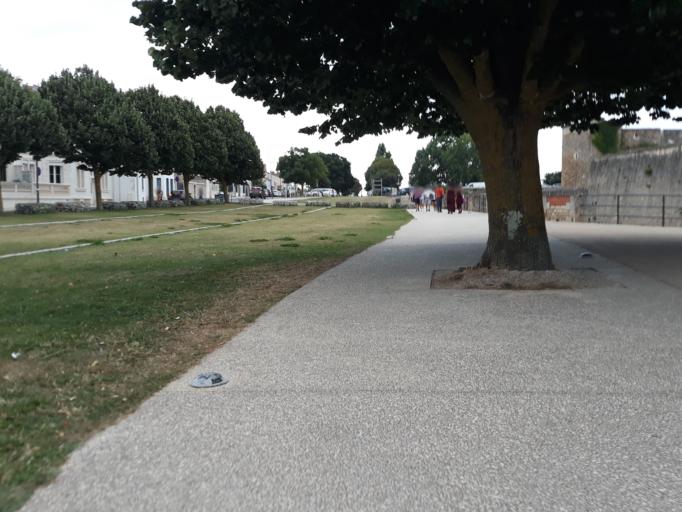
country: FR
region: Poitou-Charentes
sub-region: Departement de la Charente-Maritime
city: Fouras
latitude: 45.9867
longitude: -1.0973
